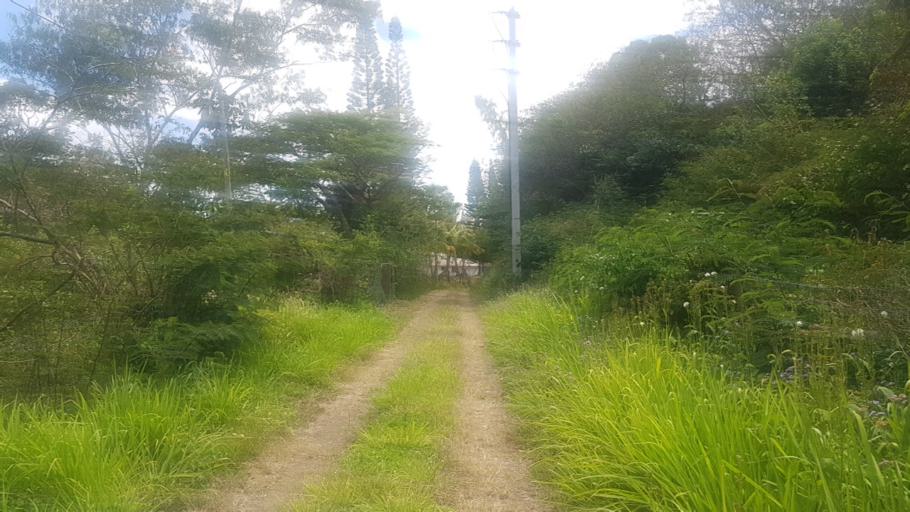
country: NC
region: South Province
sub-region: Dumbea
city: Dumbea
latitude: -22.1831
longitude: 166.4797
